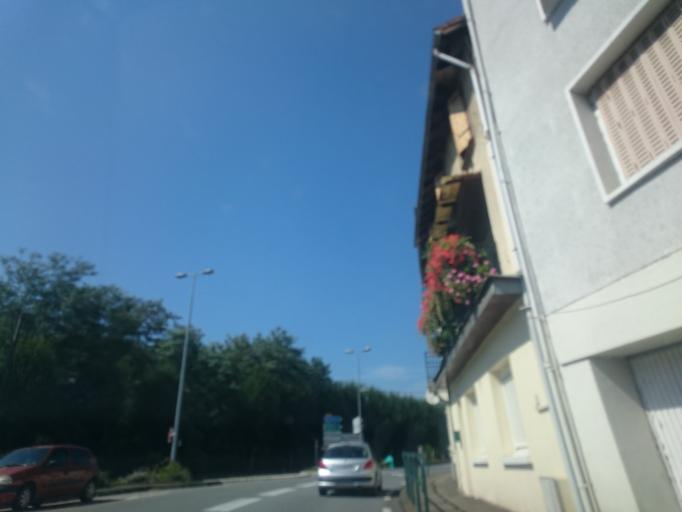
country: FR
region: Limousin
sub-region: Departement de la Correze
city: Tulle
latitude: 45.2797
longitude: 1.7689
